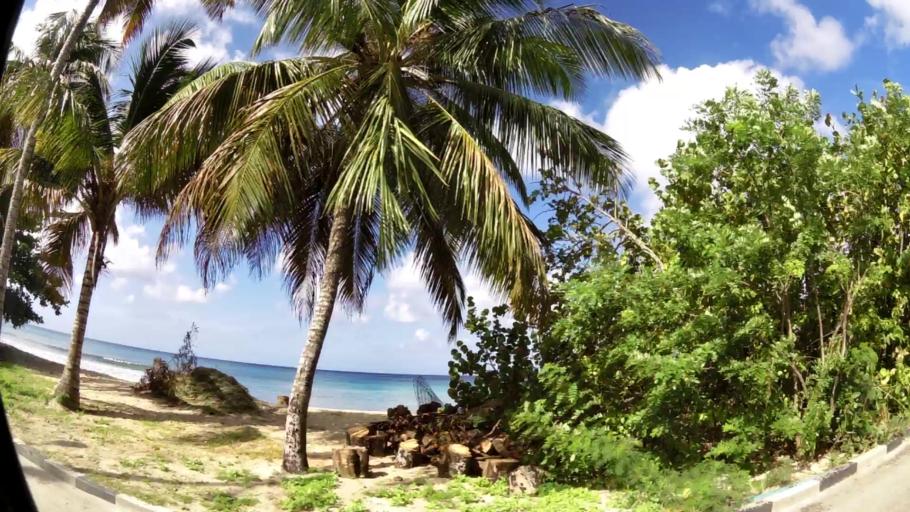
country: BB
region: Saint Lucy
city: Checker Hall
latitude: 13.2742
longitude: -59.6467
